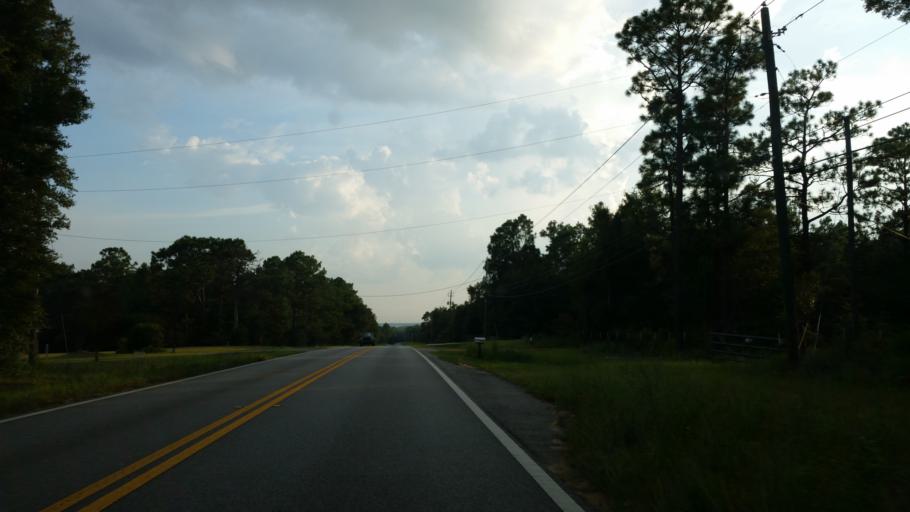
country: US
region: Florida
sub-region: Santa Rosa County
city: Pace
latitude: 30.5692
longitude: -87.1017
